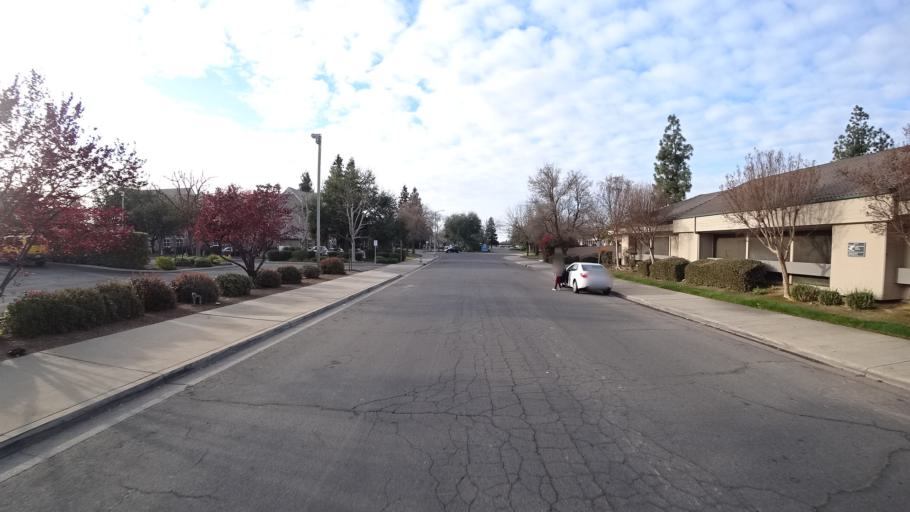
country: US
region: California
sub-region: Fresno County
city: Fresno
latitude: 36.8151
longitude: -119.7870
